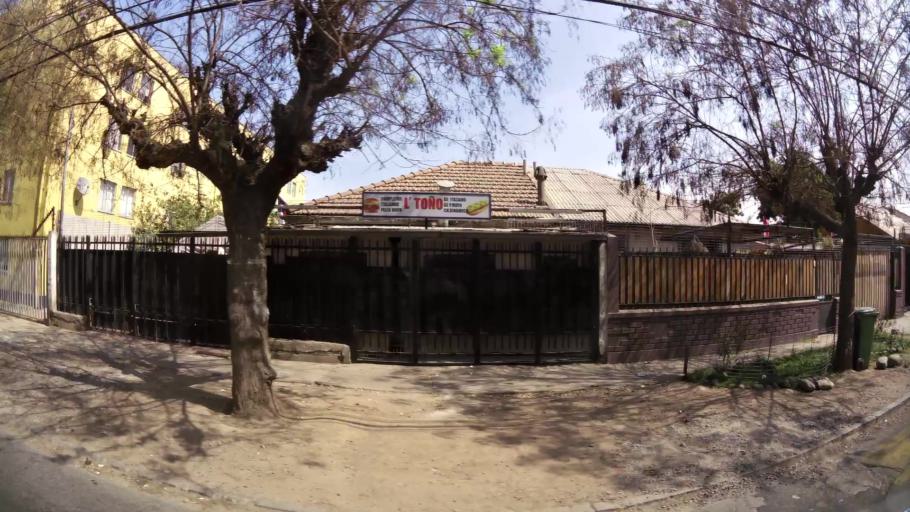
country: CL
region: Santiago Metropolitan
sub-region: Provincia de Santiago
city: Lo Prado
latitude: -33.4170
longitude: -70.6981
